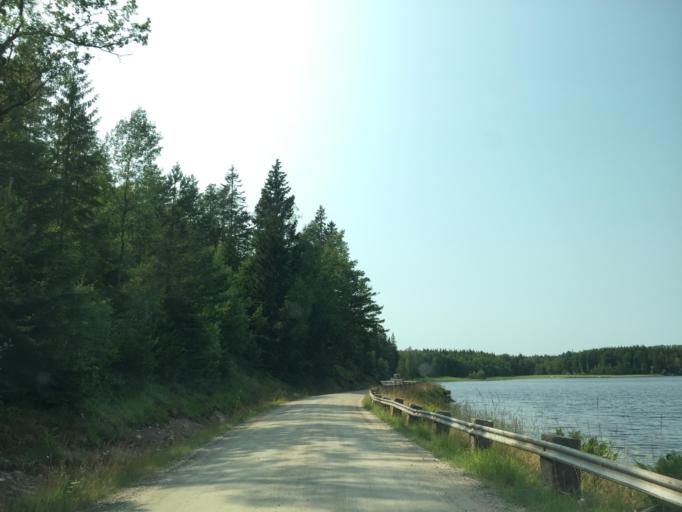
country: SE
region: Vaestra Goetaland
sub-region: Lilla Edets Kommun
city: Lilla Edet
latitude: 58.2362
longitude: 12.1096
